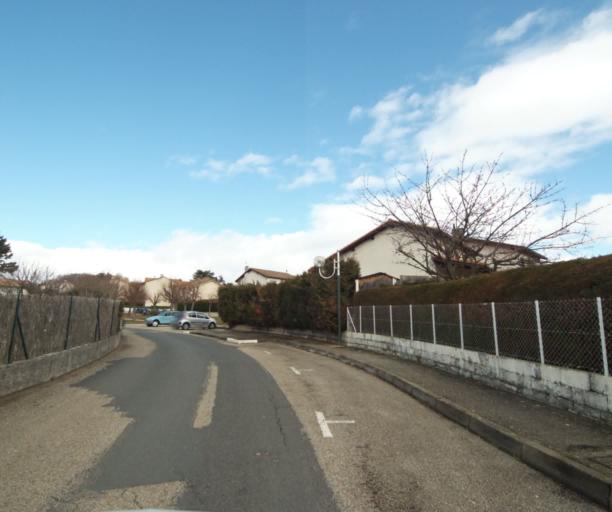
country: FR
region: Rhone-Alpes
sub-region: Departement de la Loire
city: La Talaudiere
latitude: 45.4813
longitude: 4.4279
